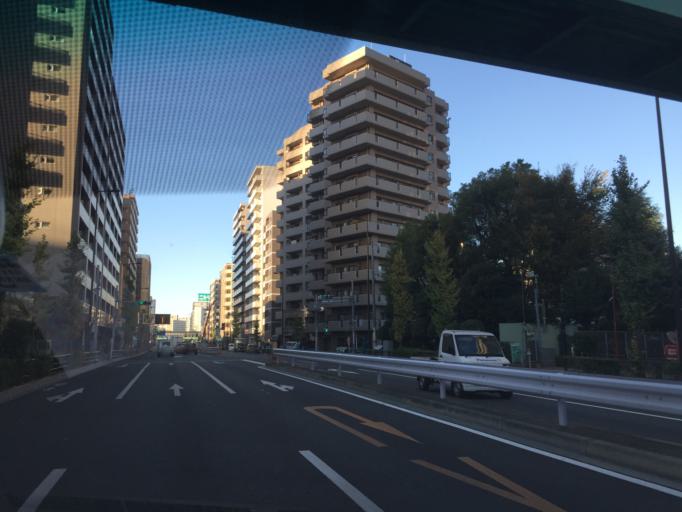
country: JP
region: Saitama
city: Kawaguchi
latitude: 35.7660
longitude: 139.7355
